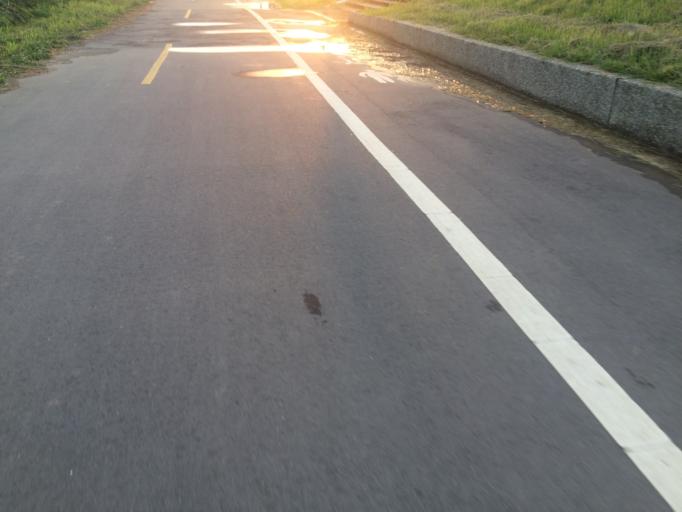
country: TW
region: Taipei
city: Taipei
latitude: 25.0766
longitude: 121.5520
